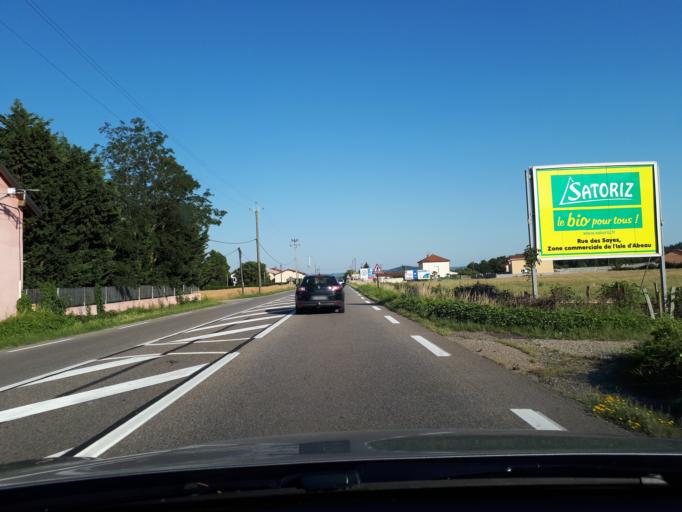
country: FR
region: Rhone-Alpes
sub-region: Departement de l'Isere
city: Grenay
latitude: 45.6699
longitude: 5.0839
